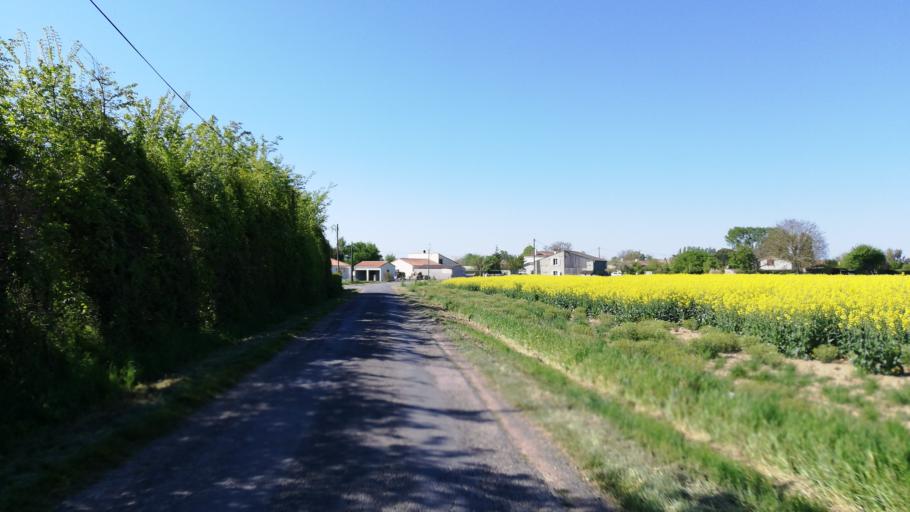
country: FR
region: Pays de la Loire
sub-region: Departement de la Vendee
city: Maillezais
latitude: 46.3253
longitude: -0.7475
